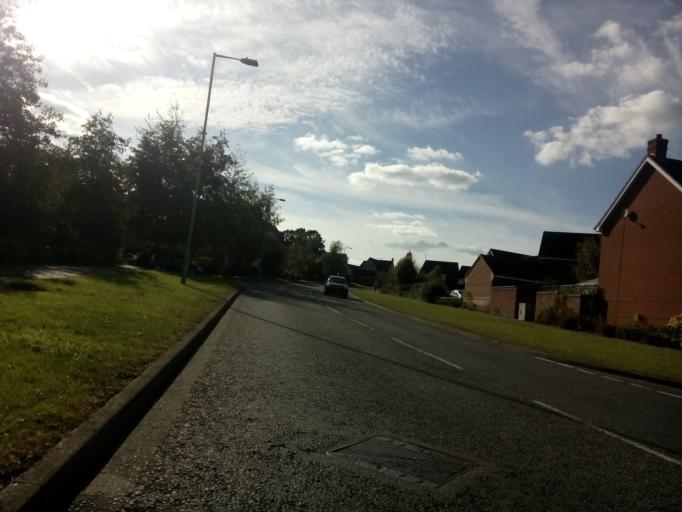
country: GB
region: England
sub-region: Suffolk
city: Ipswich
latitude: 52.0337
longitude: 1.1229
